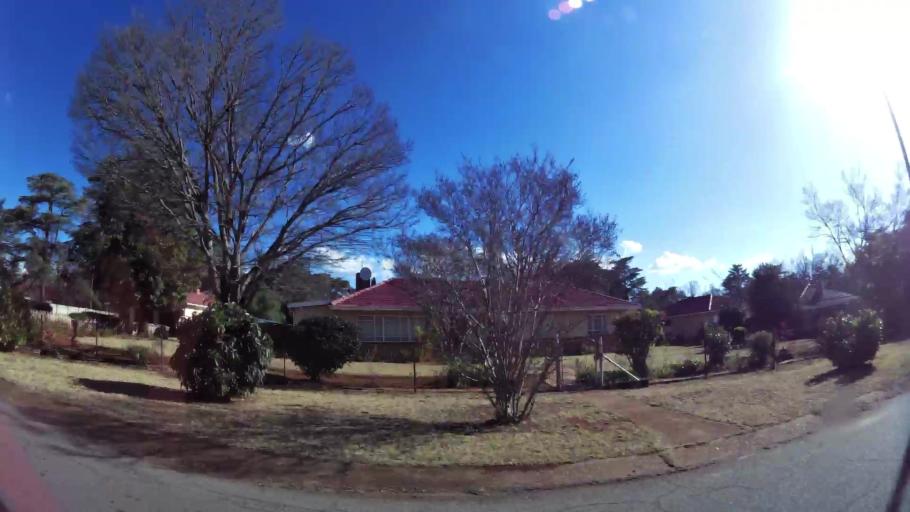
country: ZA
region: Gauteng
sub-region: West Rand District Municipality
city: Carletonville
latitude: -26.3707
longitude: 27.4093
